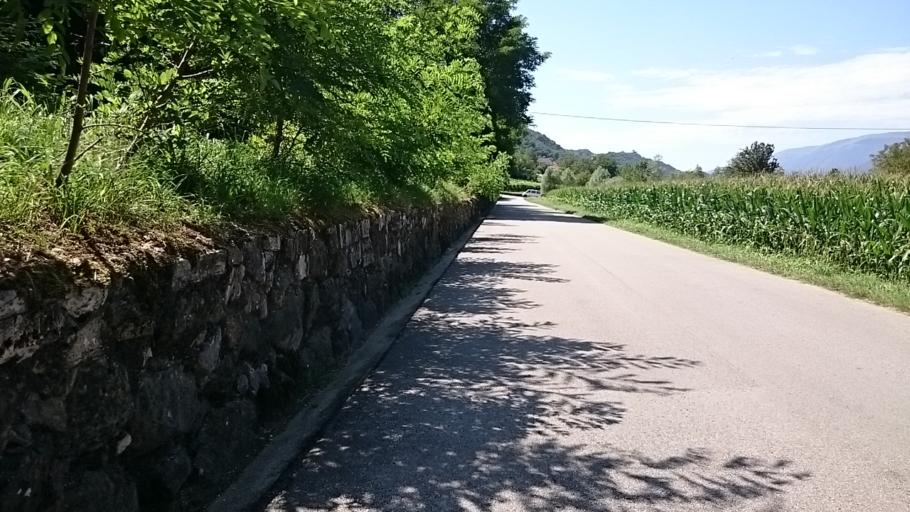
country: IT
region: Veneto
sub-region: Provincia di Treviso
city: Tarzo
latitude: 45.9813
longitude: 12.2289
